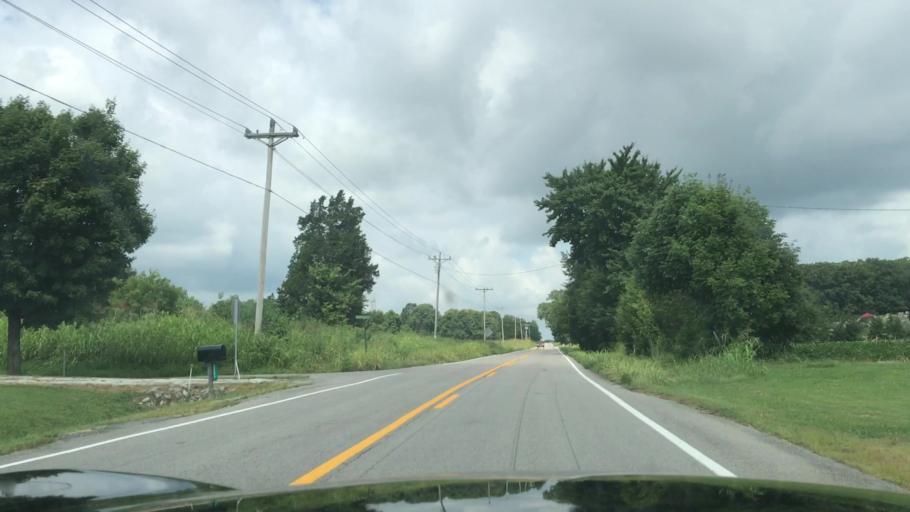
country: US
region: Kentucky
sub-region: Muhlenberg County
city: Central City
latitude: 37.1960
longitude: -86.9939
